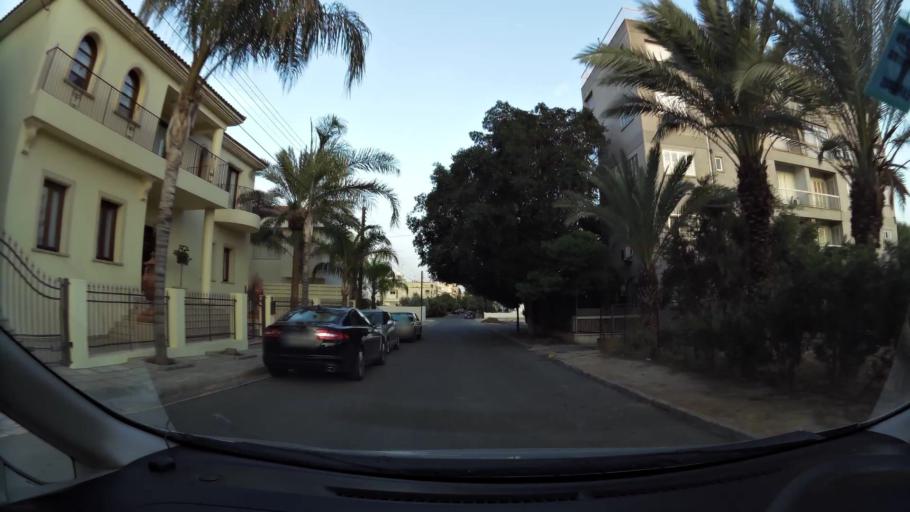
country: CY
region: Lefkosia
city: Nicosia
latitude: 35.1587
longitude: 33.3235
